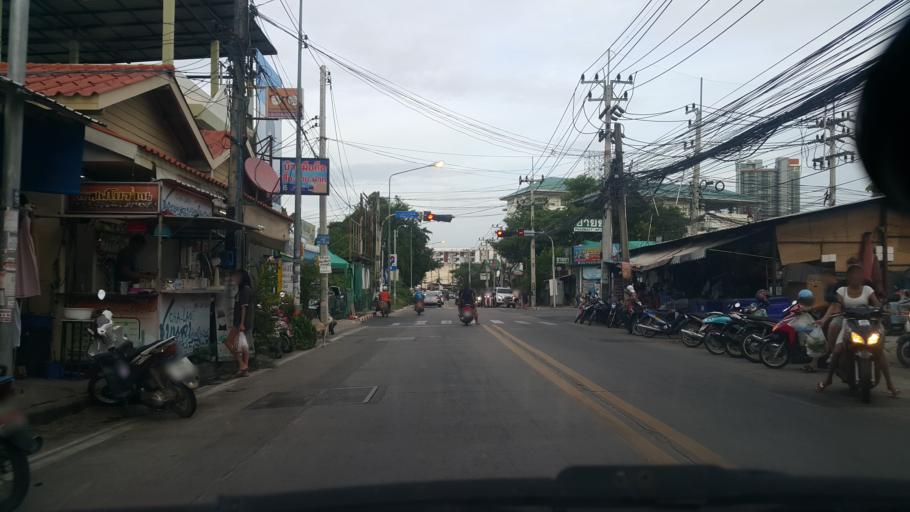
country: TH
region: Chon Buri
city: Phatthaya
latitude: 12.9558
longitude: 100.8988
